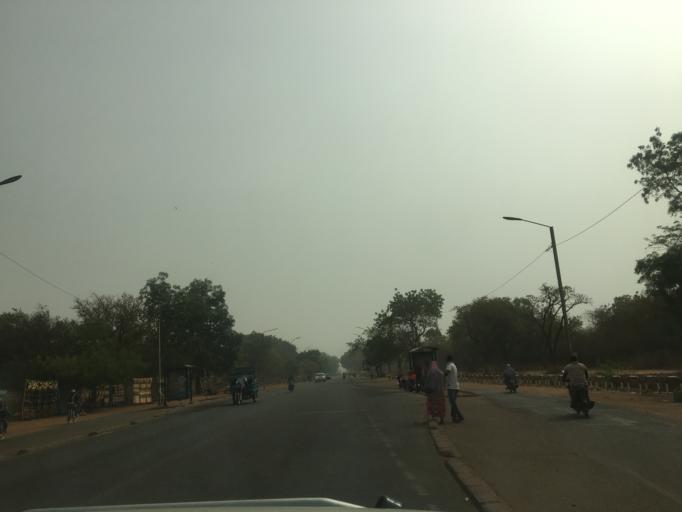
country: BF
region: Centre
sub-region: Kadiogo Province
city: Ouagadougou
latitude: 12.3976
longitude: -1.4968
